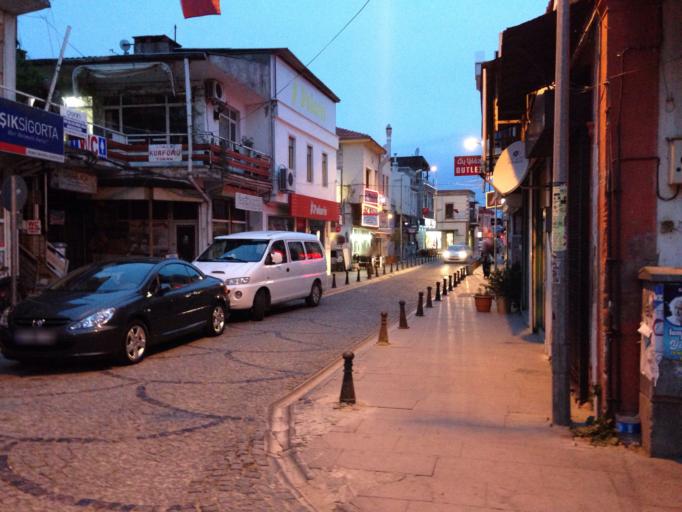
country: TR
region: Balikesir
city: Ayvalik
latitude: 39.3191
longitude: 26.6933
